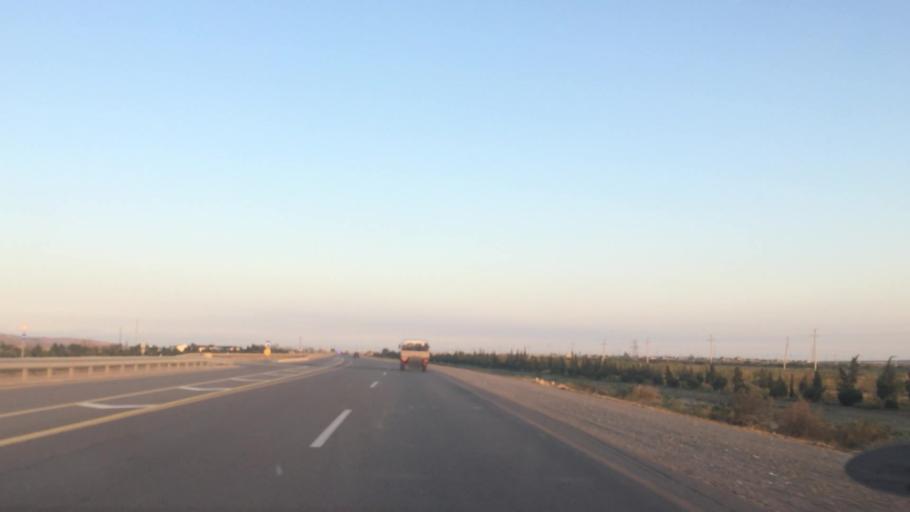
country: AZ
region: Baki
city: Qobustan
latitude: 39.9788
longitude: 49.2411
